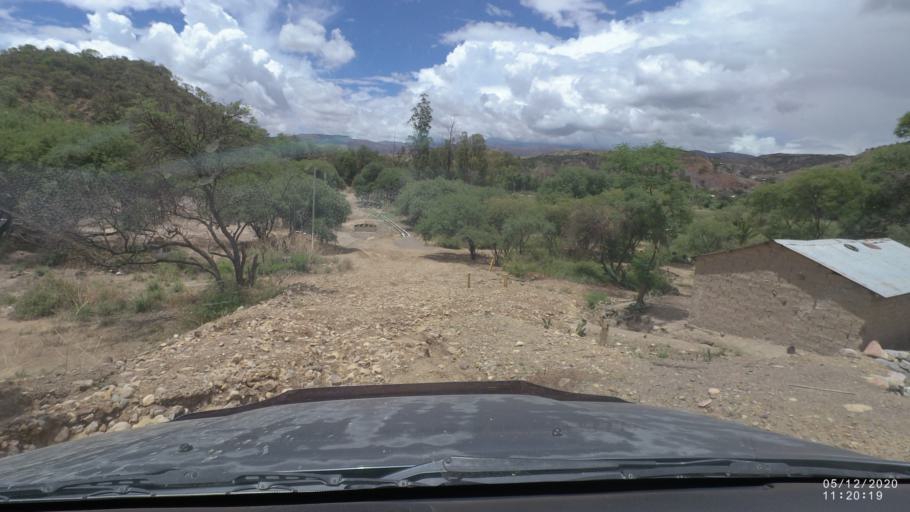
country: BO
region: Cochabamba
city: Sipe Sipe
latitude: -17.5518
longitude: -66.3378
